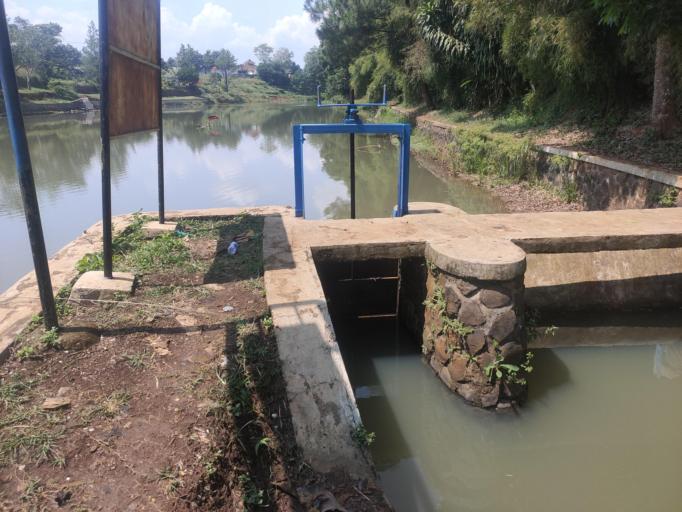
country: ID
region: West Java
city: Ciampea
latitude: -6.5247
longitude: 106.6995
